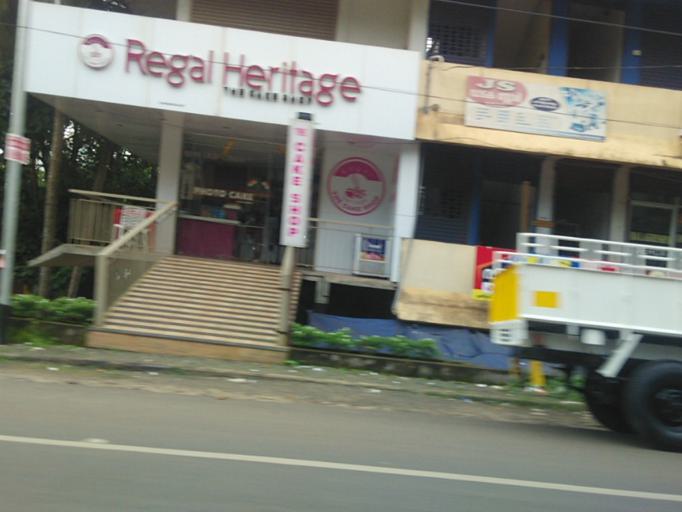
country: IN
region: Kerala
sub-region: Kozhikode
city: Kunnamangalam
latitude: 11.3039
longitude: 75.8756
